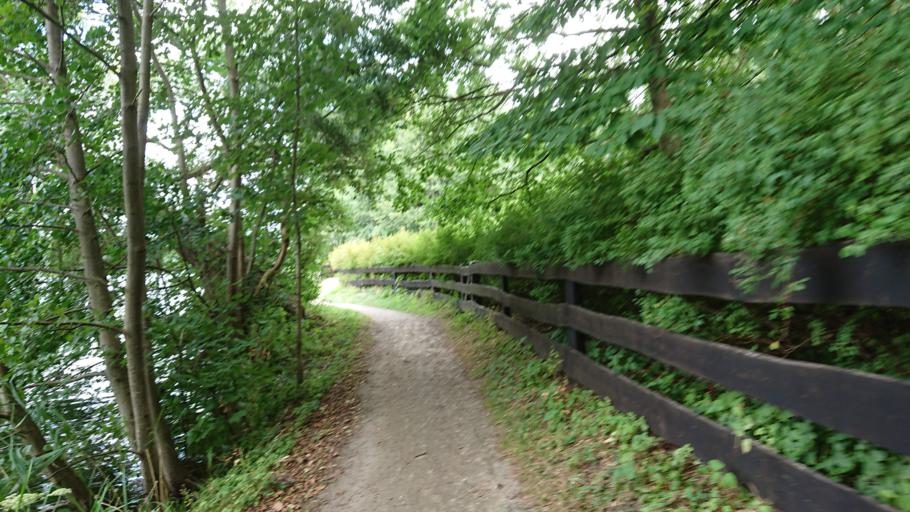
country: DE
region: Schleswig-Holstein
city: Schmilau
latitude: 53.6783
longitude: 10.7590
